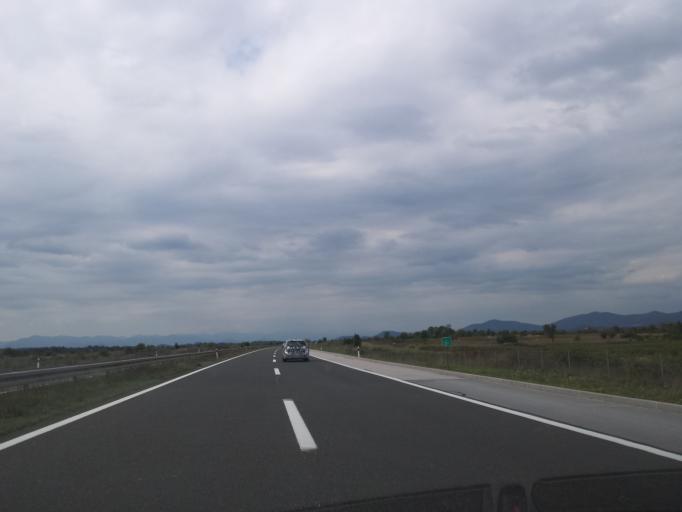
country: HR
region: Licko-Senjska
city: Gospic
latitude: 44.4829
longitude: 15.5547
